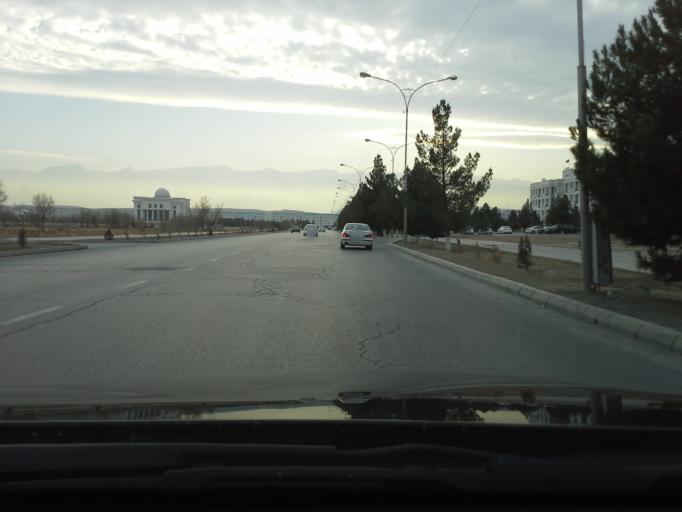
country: TM
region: Ahal
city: Ashgabat
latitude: 37.9968
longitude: 58.3253
